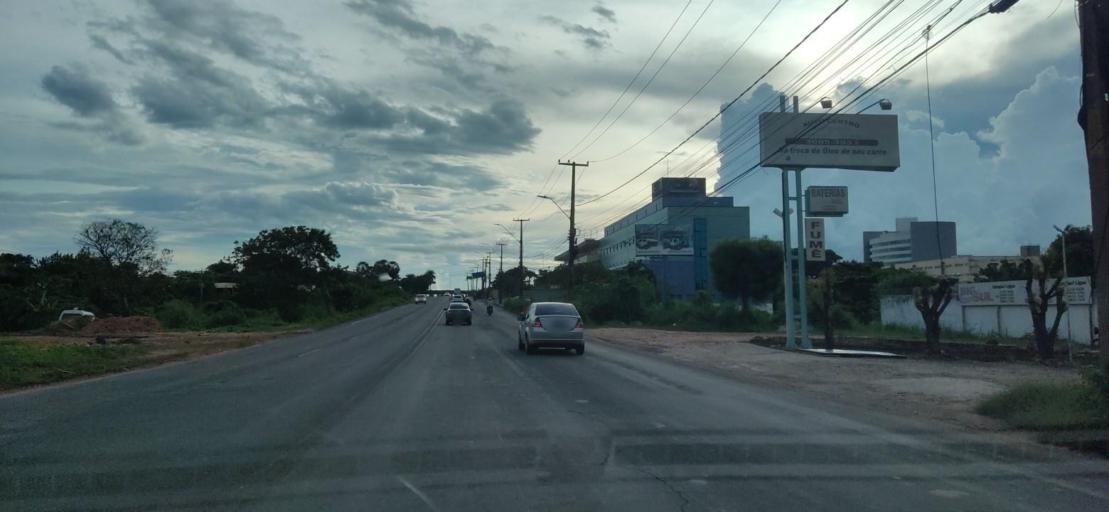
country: BR
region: Piaui
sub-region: Teresina
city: Teresina
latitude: -5.1209
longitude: -42.7912
